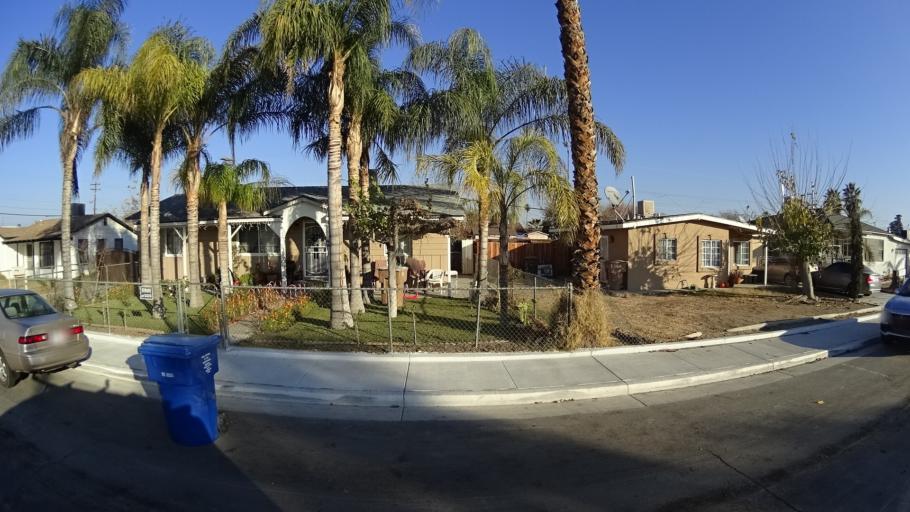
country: US
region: California
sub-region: Kern County
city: Greenfield
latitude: 35.3032
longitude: -119.0003
